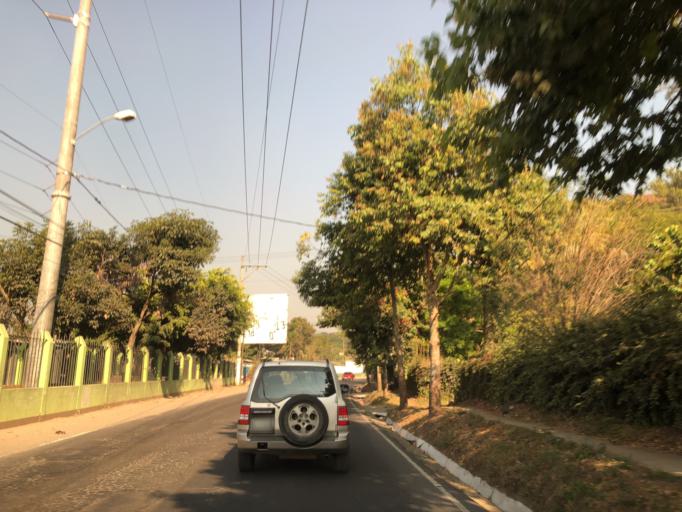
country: GT
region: Guatemala
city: Villa Canales
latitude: 14.4894
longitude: -90.5354
